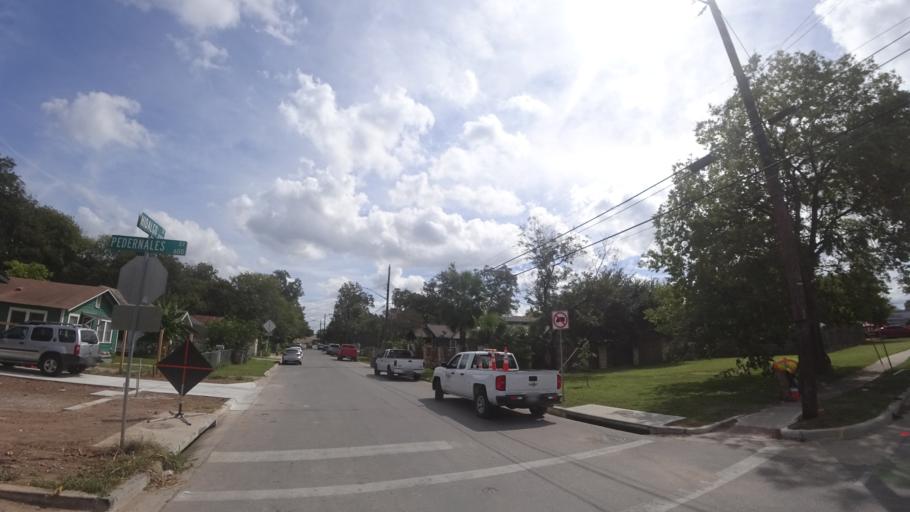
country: US
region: Texas
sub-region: Travis County
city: Austin
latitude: 30.2598
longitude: -97.7142
